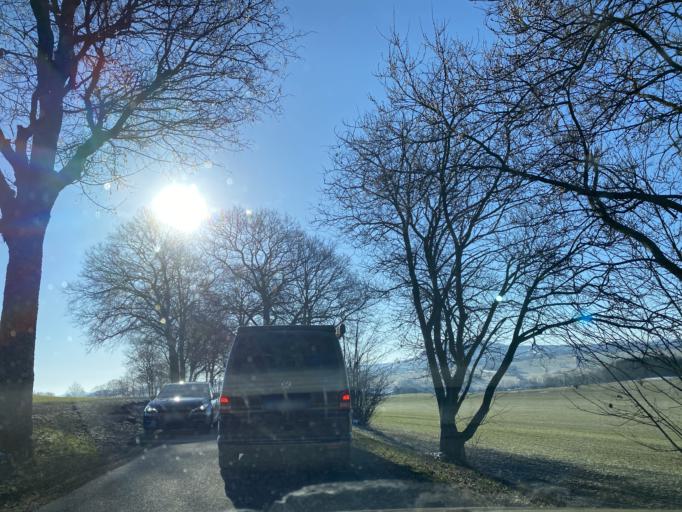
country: DE
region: Saxony
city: Wiesa
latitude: 50.6204
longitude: 12.9989
